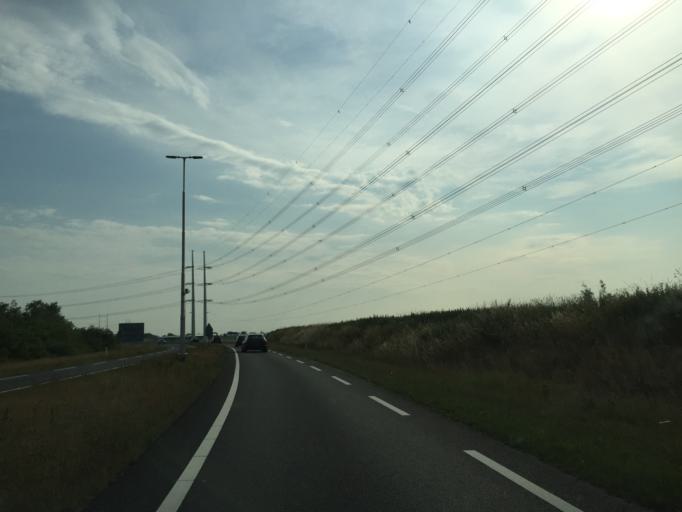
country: NL
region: South Holland
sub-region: Gemeente Zoetermeer
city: Zoetermeer
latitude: 52.0318
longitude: 4.4747
